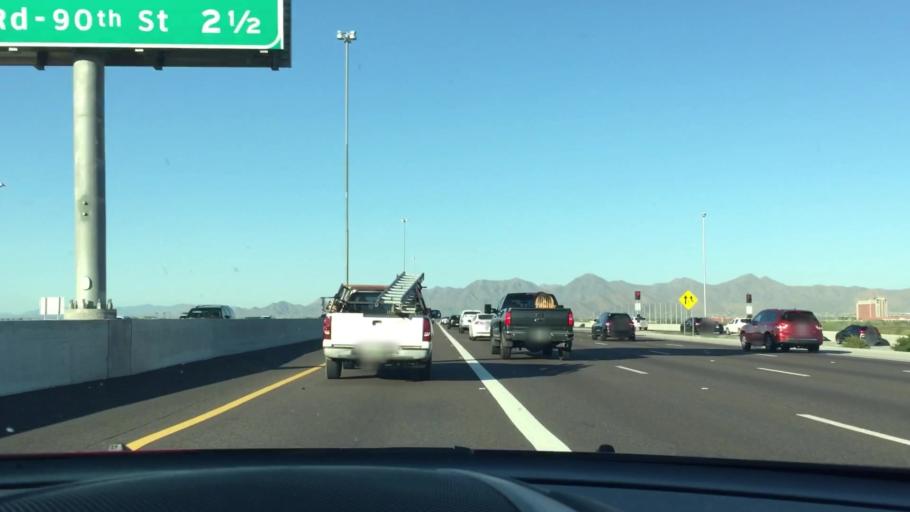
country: US
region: Arizona
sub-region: Maricopa County
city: Scottsdale
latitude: 33.5262
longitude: -111.8857
